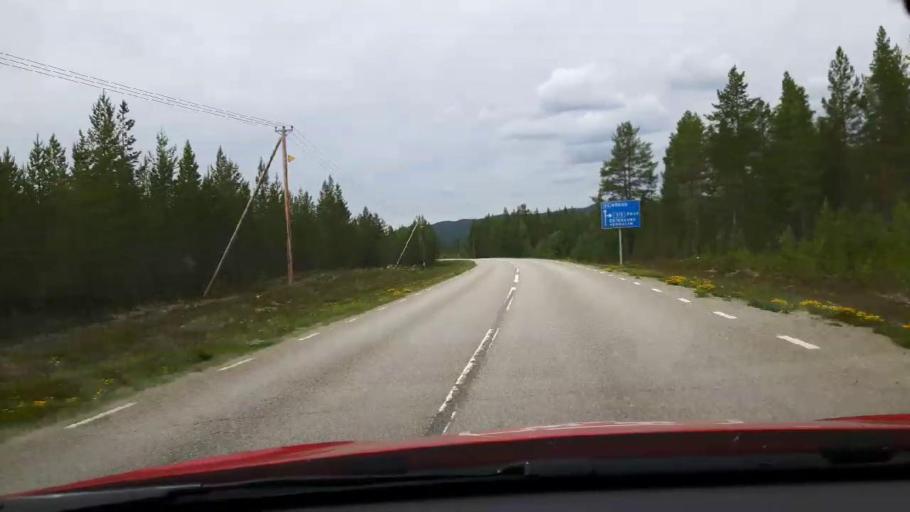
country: SE
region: Jaemtland
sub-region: Harjedalens Kommun
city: Sveg
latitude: 62.4036
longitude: 13.7372
